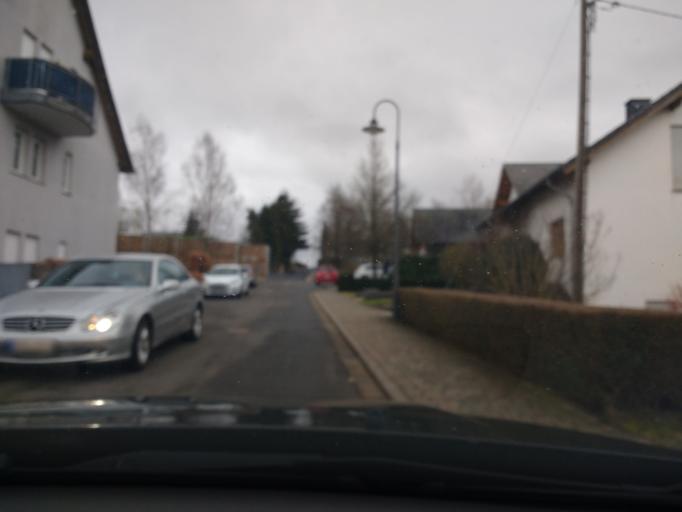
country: DE
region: Rheinland-Pfalz
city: Kell am See
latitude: 49.6313
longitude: 6.8227
